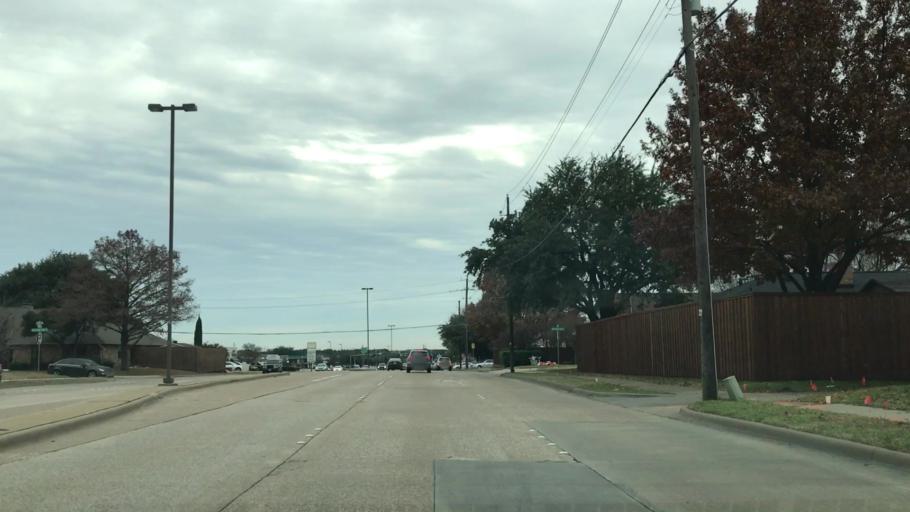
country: US
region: Texas
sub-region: Dallas County
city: Carrollton
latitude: 33.0153
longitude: -96.8871
